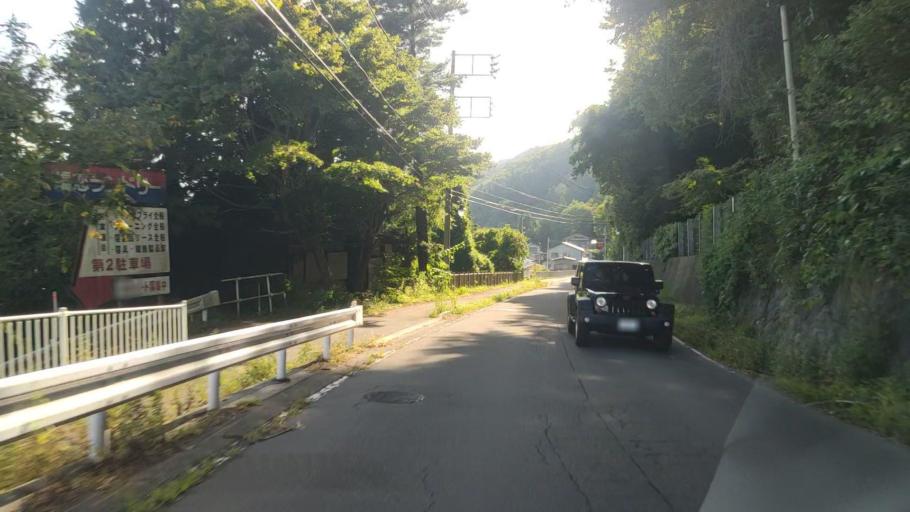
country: JP
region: Nagano
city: Komoro
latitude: 36.5401
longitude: 138.5532
